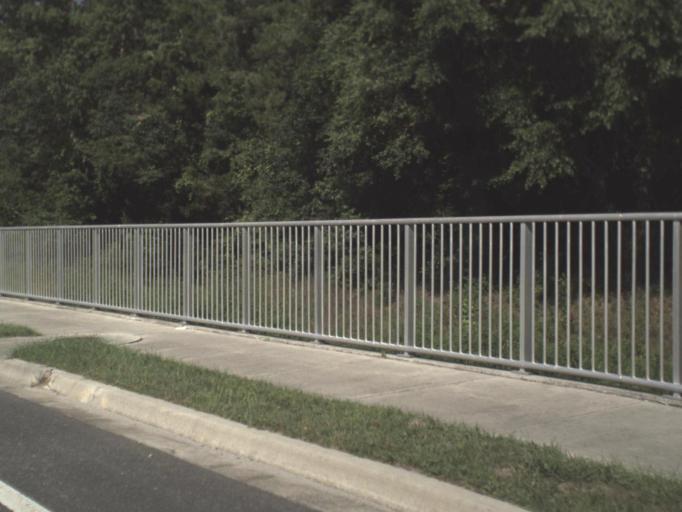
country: US
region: Florida
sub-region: Columbia County
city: Lake City
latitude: 30.1136
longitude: -82.6581
